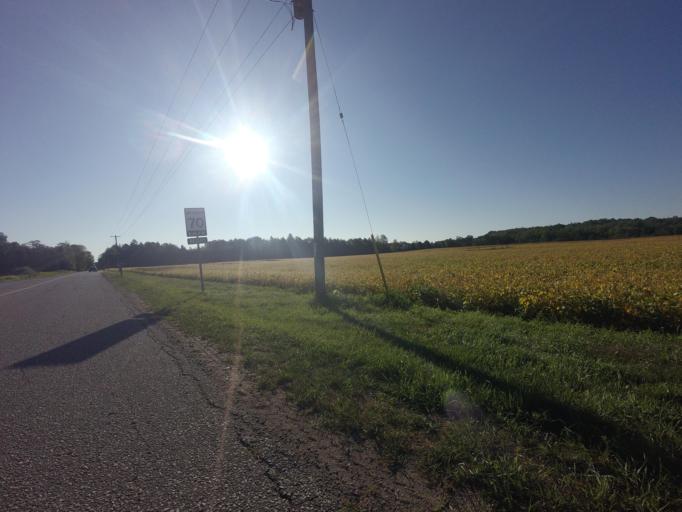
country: CA
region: Ontario
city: Bradford West Gwillimbury
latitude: 44.0483
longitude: -79.7457
